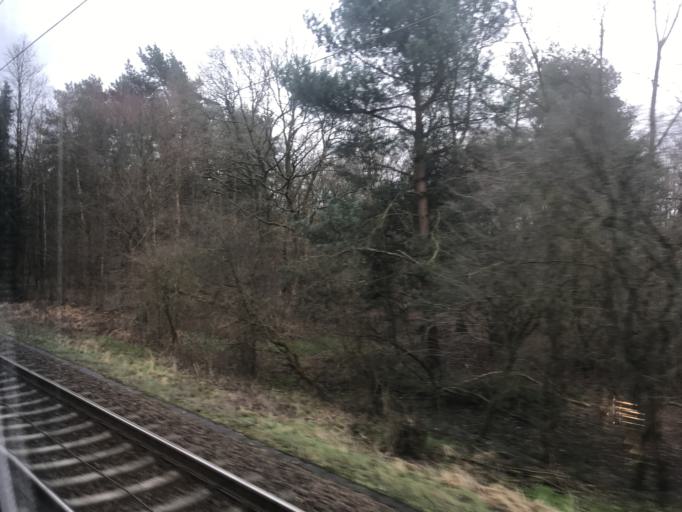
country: DE
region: Lower Saxony
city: Ribbesbuttel
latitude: 52.4567
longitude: 10.5259
